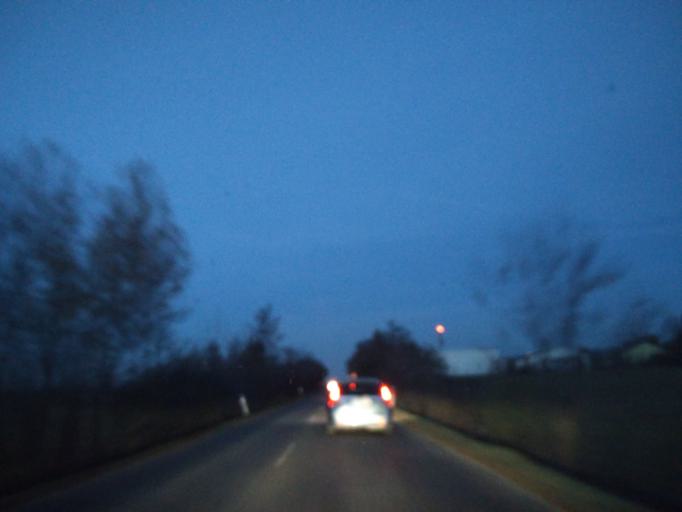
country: HU
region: Pest
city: Budakeszi
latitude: 47.4879
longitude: 18.9074
